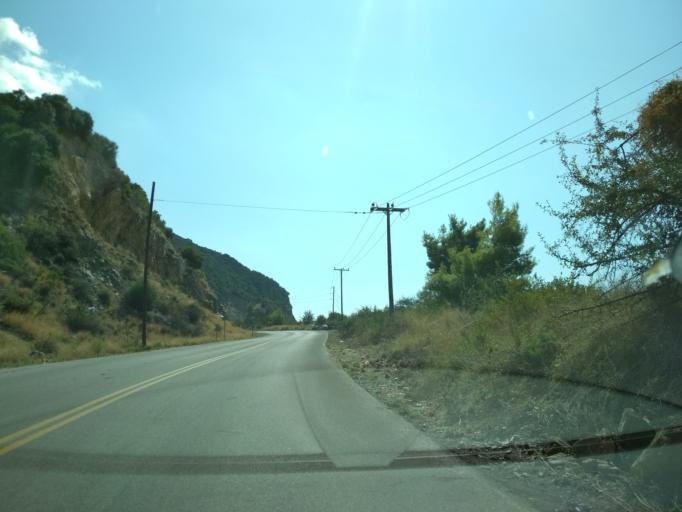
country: GR
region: Central Greece
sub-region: Nomos Evvoias
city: Roviai
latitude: 38.8520
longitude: 23.1427
